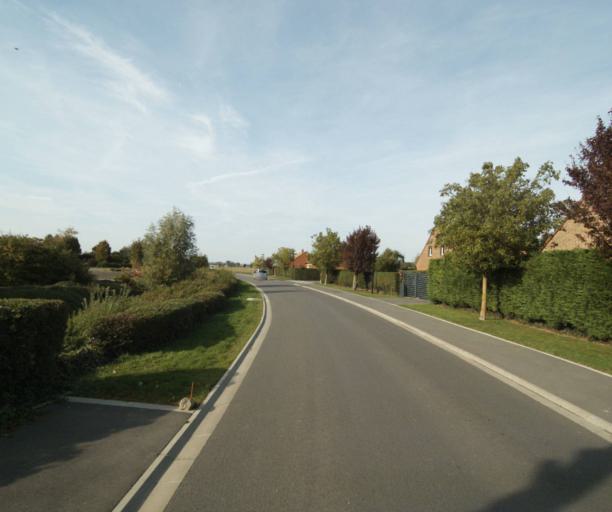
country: FR
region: Nord-Pas-de-Calais
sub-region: Departement du Nord
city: Fournes-en-Weppes
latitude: 50.5875
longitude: 2.8832
